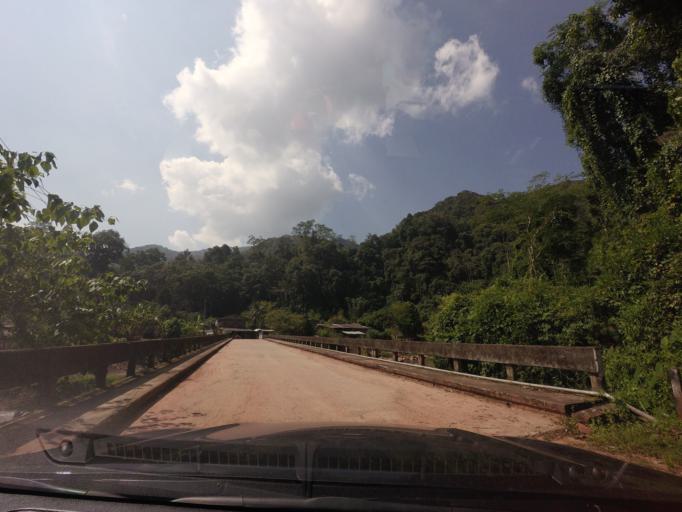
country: TH
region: Nan
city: Bo Kluea
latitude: 19.1930
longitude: 101.1984
